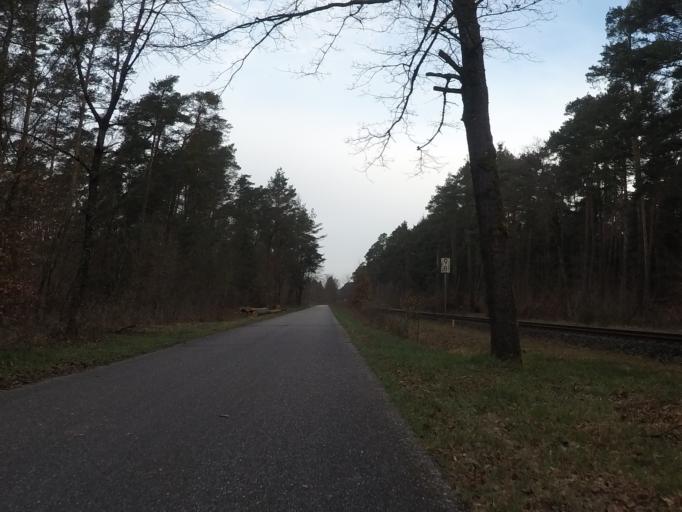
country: DE
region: Rheinland-Pfalz
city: Worth am Rhein
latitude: 49.0658
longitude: 8.2292
